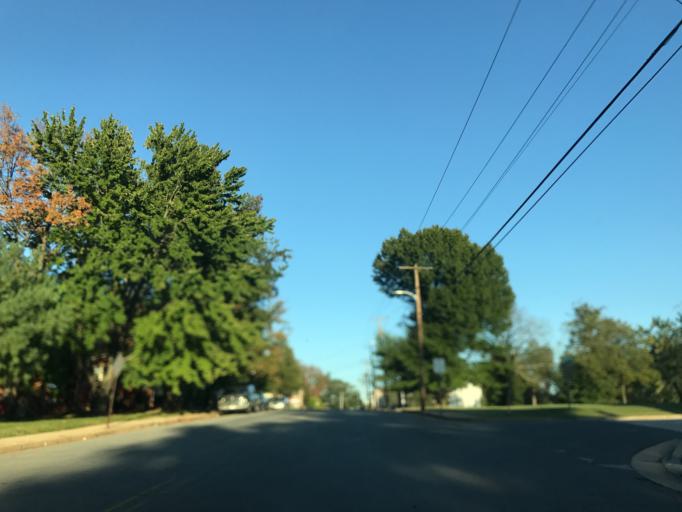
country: US
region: Maryland
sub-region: Baltimore County
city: Rosedale
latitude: 39.3369
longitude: -76.5363
